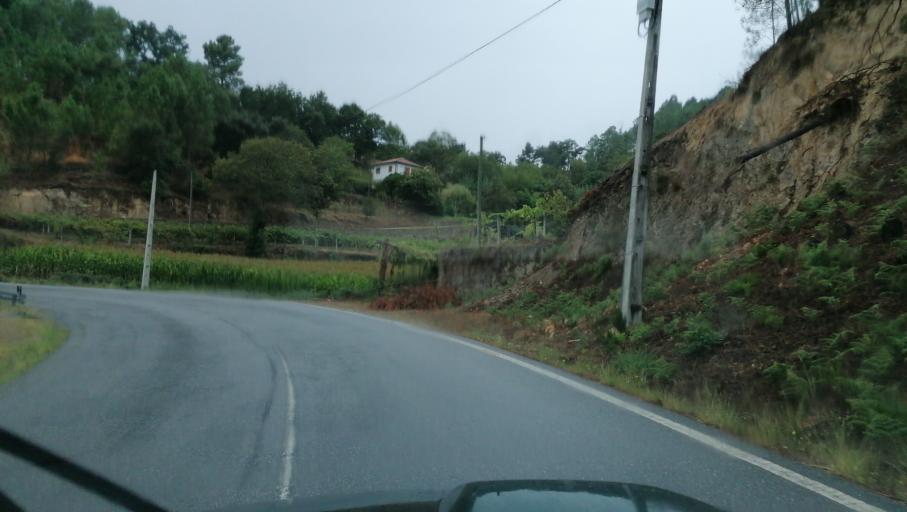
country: PT
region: Braga
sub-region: Cabeceiras de Basto
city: Cabeceiras de Basto
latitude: 41.4958
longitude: -7.9461
